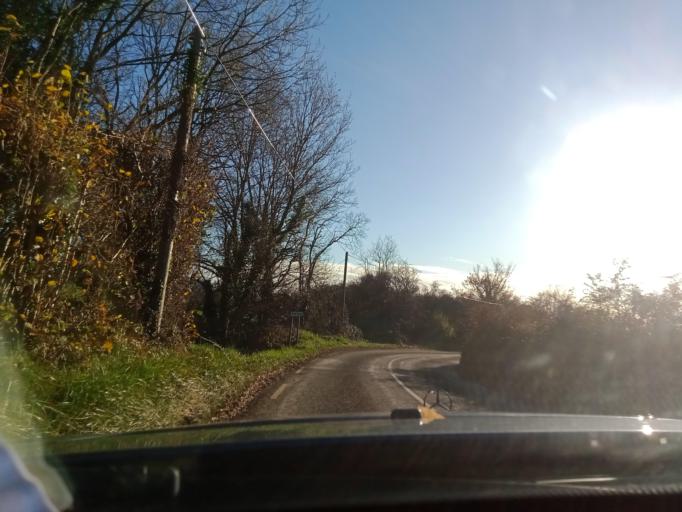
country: IE
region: Leinster
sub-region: Kilkenny
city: Piltown
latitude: 52.3927
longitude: -7.3494
